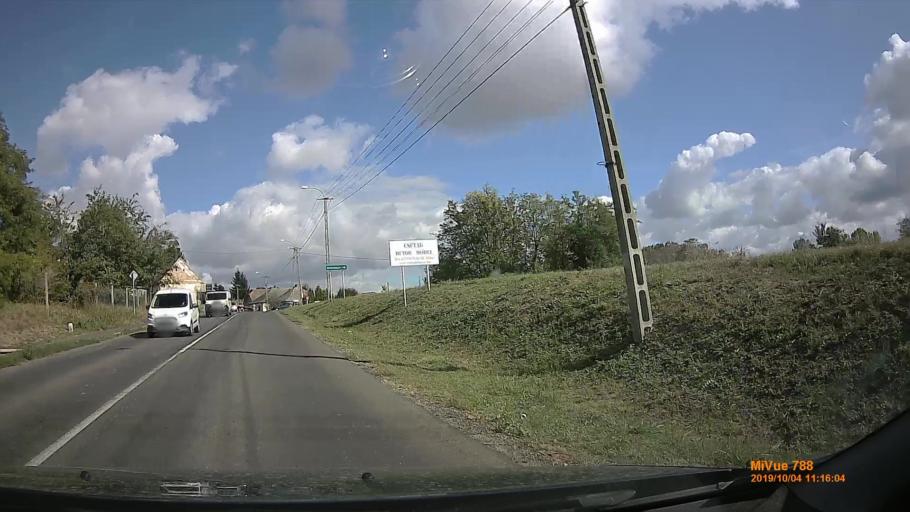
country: HU
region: Somogy
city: Kaposvar
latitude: 46.4527
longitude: 17.8047
